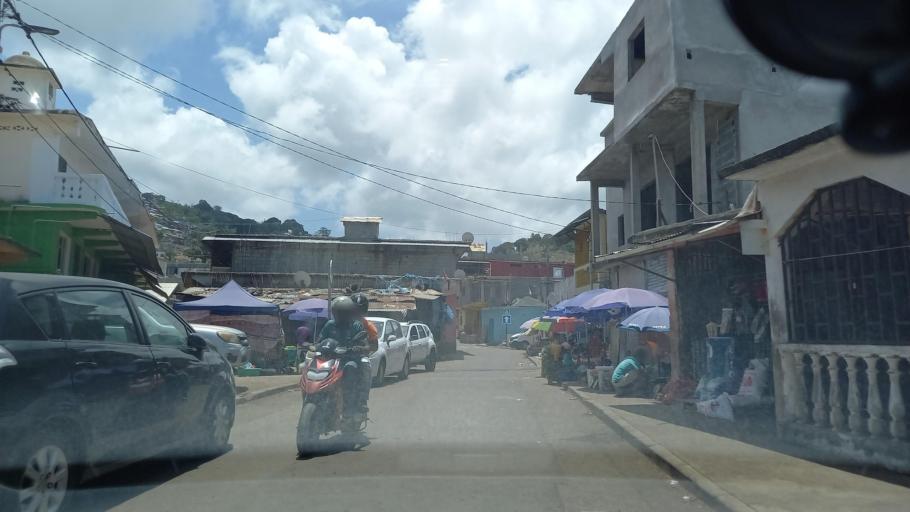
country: YT
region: Mamoudzou
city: Mamoudzou
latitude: -12.7746
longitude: 45.2222
